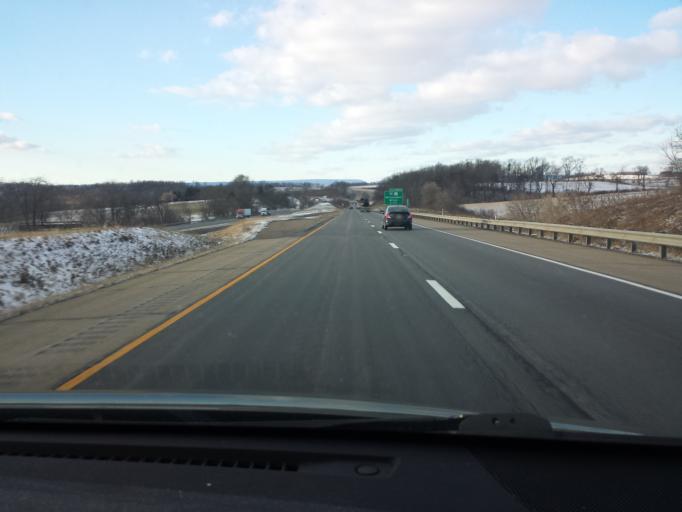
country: US
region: Pennsylvania
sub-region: Northumberland County
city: Milton
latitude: 41.0329
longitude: -76.8064
